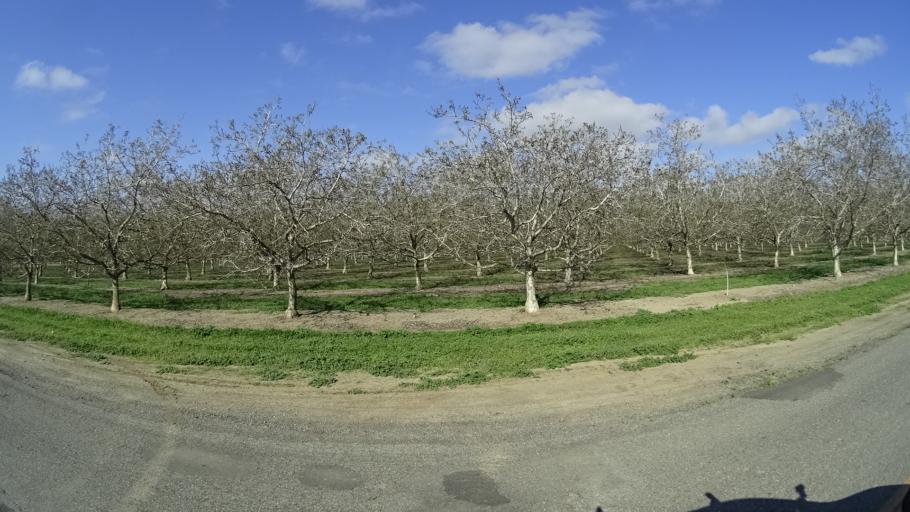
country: US
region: California
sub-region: Glenn County
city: Willows
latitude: 39.4653
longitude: -121.9678
